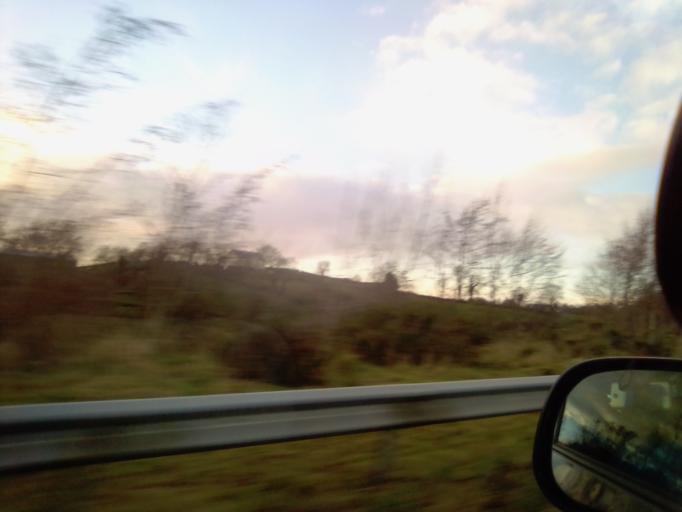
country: IE
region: Ulster
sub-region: County Monaghan
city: Castleblayney
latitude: 54.1845
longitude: -6.8229
